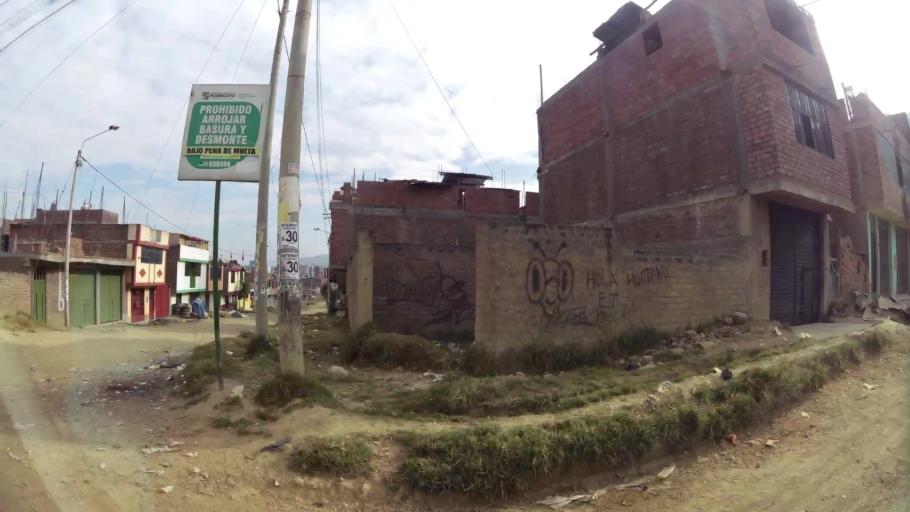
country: PE
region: Junin
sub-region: Provincia de Huancayo
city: Huancayo
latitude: -12.0534
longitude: -75.1871
